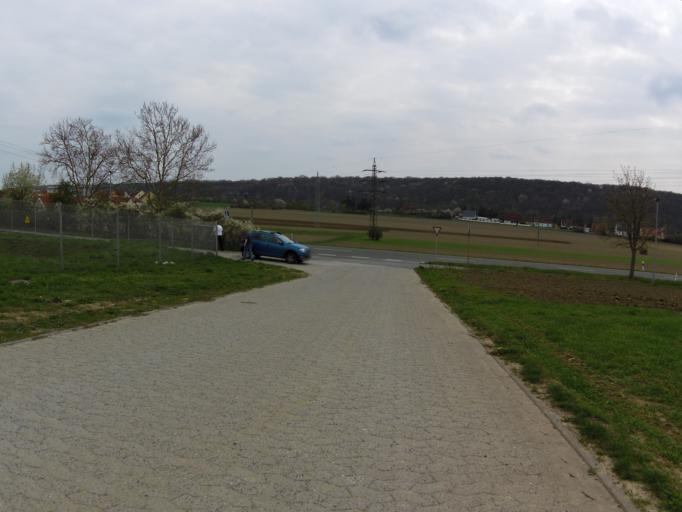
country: DE
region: Bavaria
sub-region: Regierungsbezirk Unterfranken
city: Rottendorf
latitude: 49.7916
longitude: 10.0143
